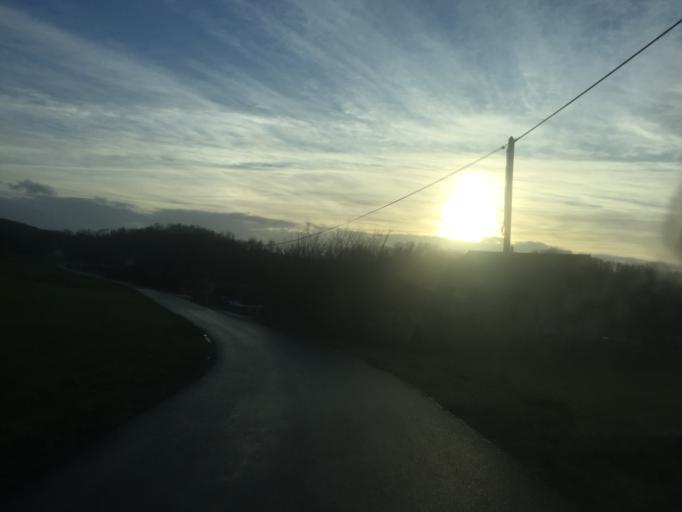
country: FR
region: Franche-Comte
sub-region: Departement du Jura
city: Dampierre
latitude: 47.1356
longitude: 5.7183
